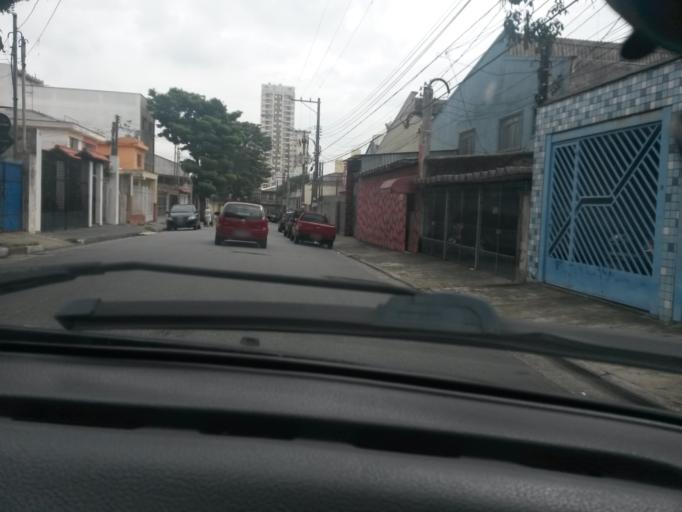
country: BR
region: Sao Paulo
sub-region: Sao Caetano Do Sul
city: Sao Caetano do Sul
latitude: -23.6259
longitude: -46.6075
